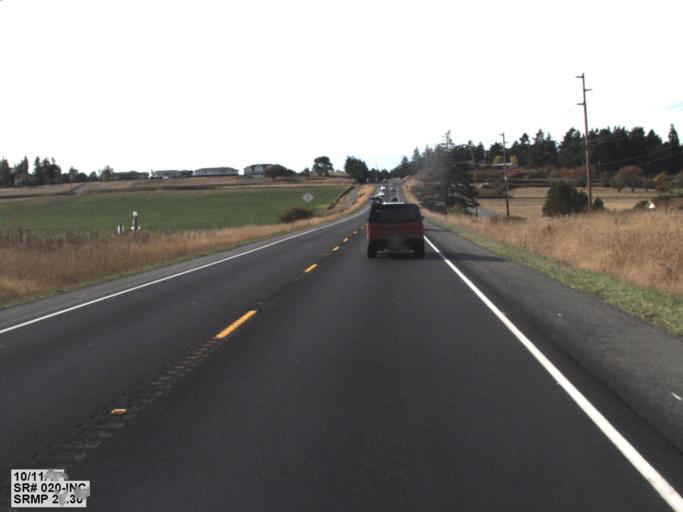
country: US
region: Washington
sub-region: Island County
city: Coupeville
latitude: 48.2123
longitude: -122.6964
